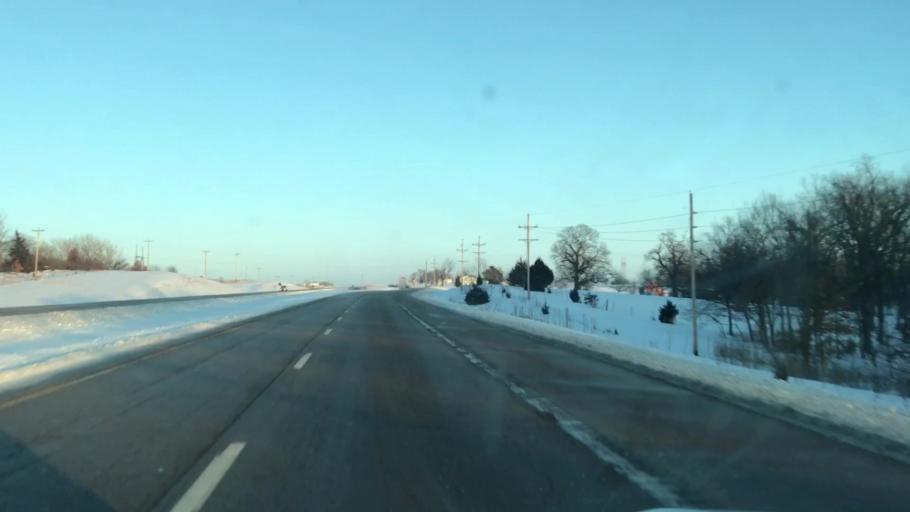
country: US
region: Missouri
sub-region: Clinton County
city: Cameron
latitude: 39.7548
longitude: -94.3136
